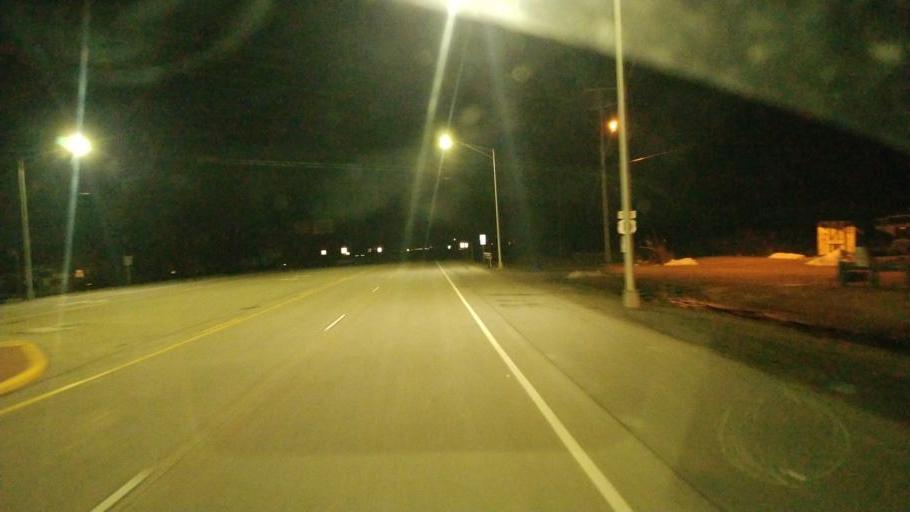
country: US
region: Wisconsin
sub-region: Wood County
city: Marshfield
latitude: 44.5987
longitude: -90.1803
